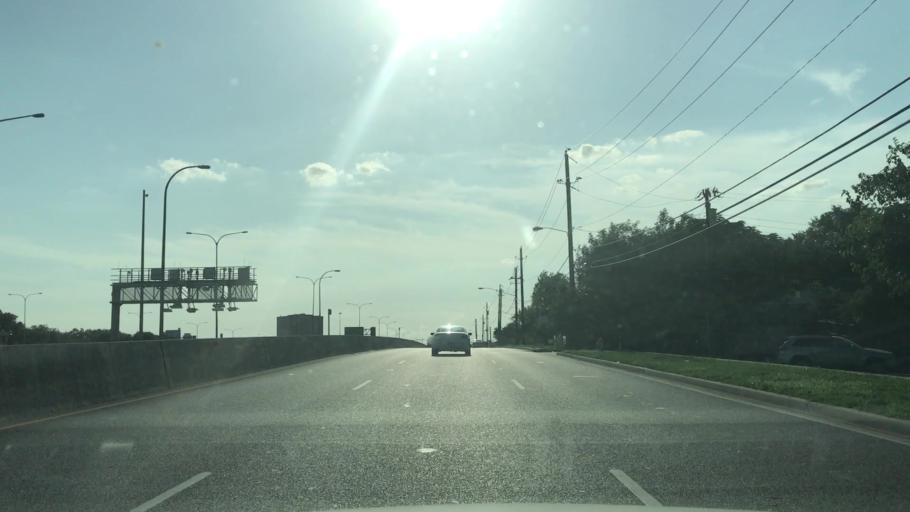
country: US
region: Texas
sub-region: Dallas County
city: Addison
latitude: 32.9257
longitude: -96.7925
